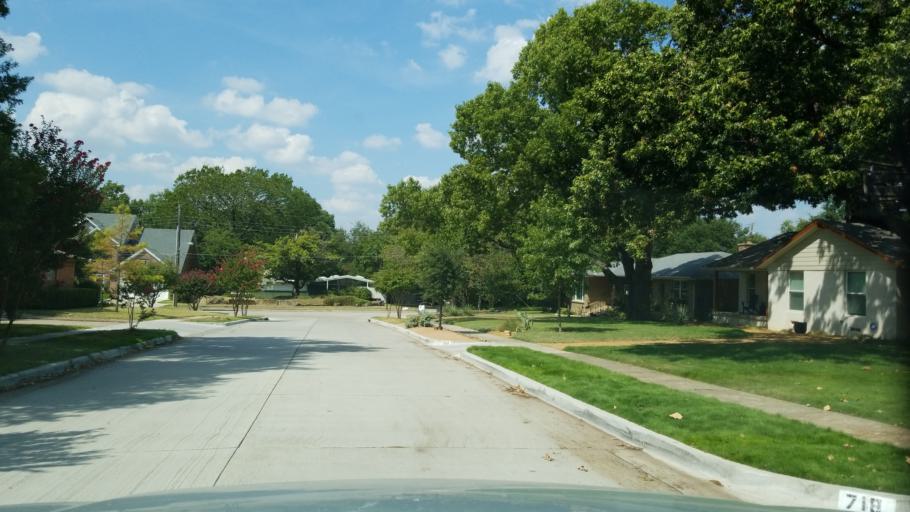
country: US
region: Texas
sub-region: Dallas County
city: Richardson
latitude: 32.9577
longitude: -96.7460
